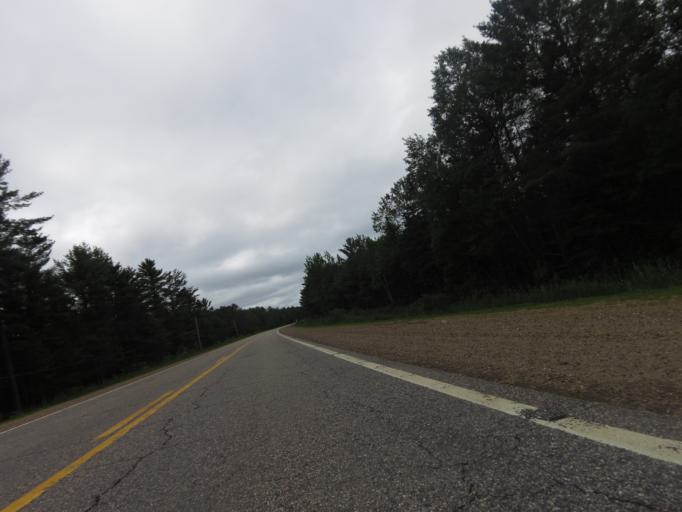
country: CA
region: Quebec
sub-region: Outaouais
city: Shawville
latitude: 45.8642
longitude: -76.4075
